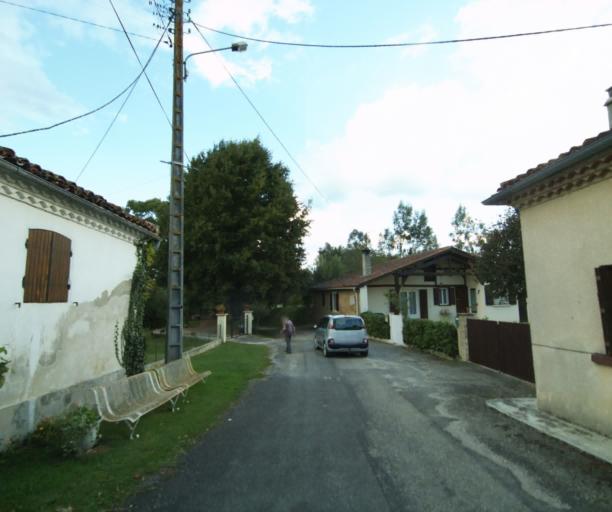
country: FR
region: Midi-Pyrenees
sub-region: Departement du Gers
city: Cazaubon
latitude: 43.9322
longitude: -0.0851
